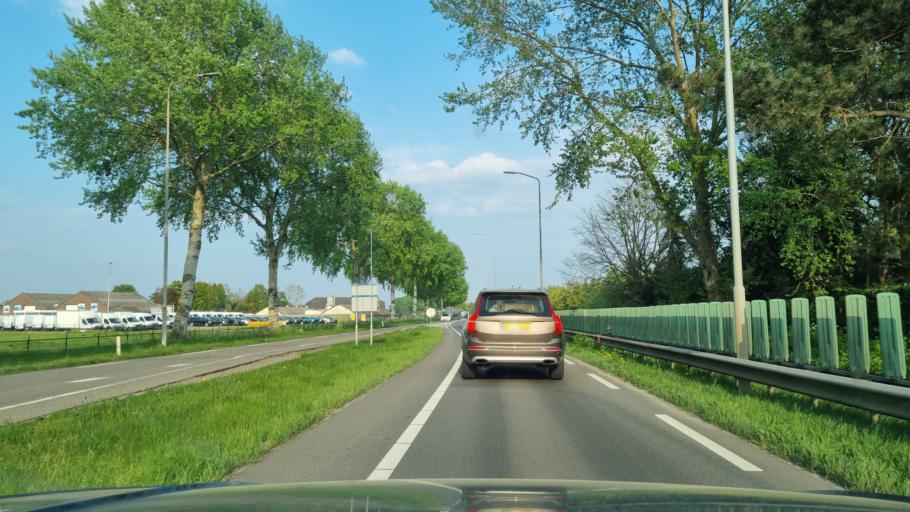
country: NL
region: North Brabant
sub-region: Gemeente Cuijk
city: Cuijk
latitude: 51.7265
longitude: 5.8274
